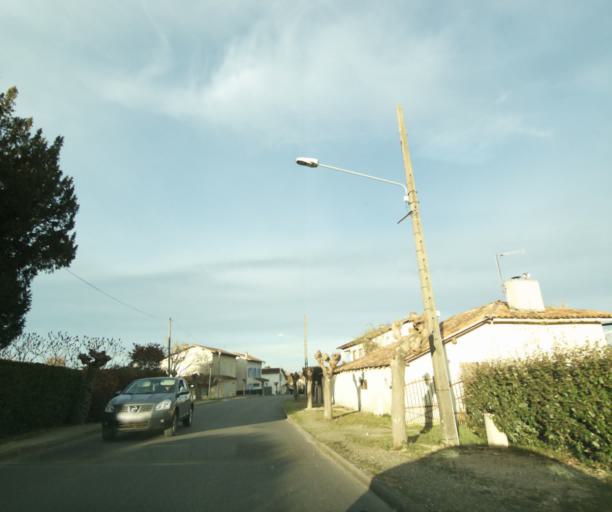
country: FR
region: Aquitaine
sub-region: Departement des Landes
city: Gabarret
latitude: 43.9825
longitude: 0.0088
